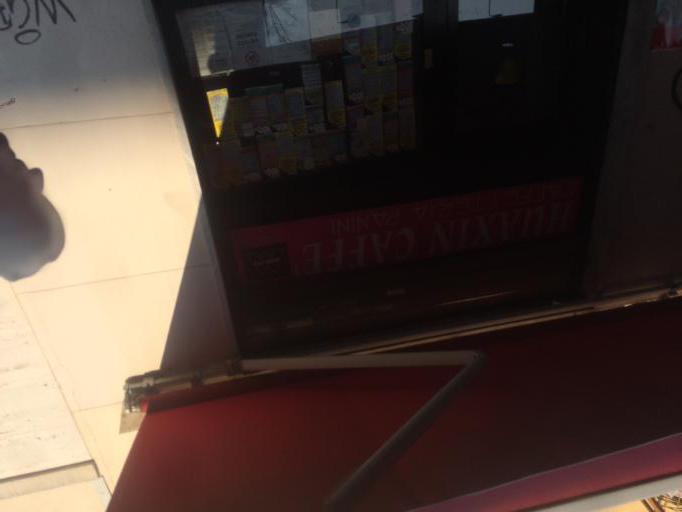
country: IT
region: Lombardy
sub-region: Citta metropolitana di Milano
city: Romano Banco
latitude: 45.4686
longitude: 9.1375
